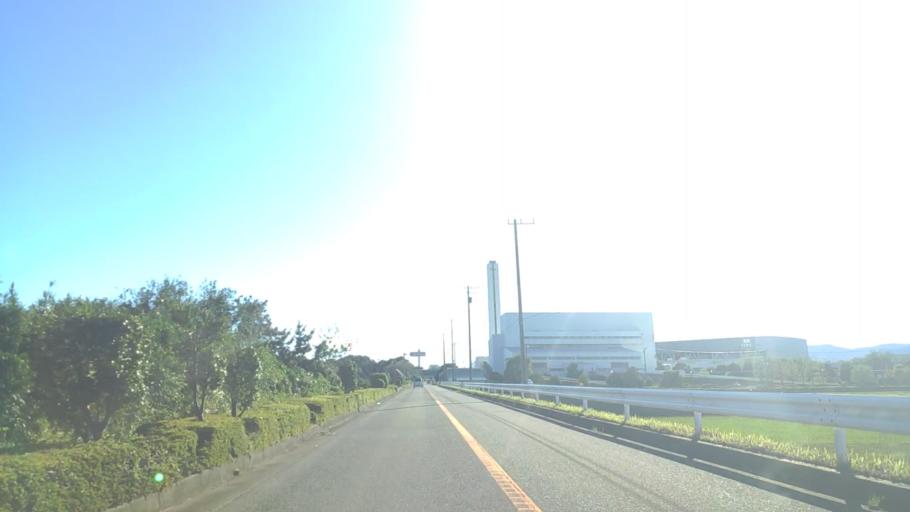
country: JP
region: Kanagawa
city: Atsugi
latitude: 35.4602
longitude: 139.3761
